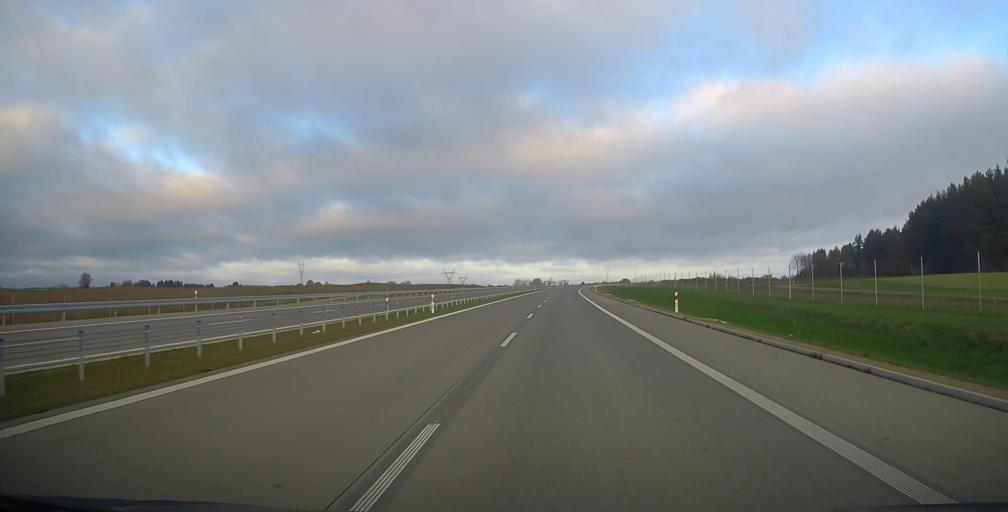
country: PL
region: Podlasie
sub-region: Powiat grajewski
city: Szczuczyn
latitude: 53.6283
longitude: 22.2984
